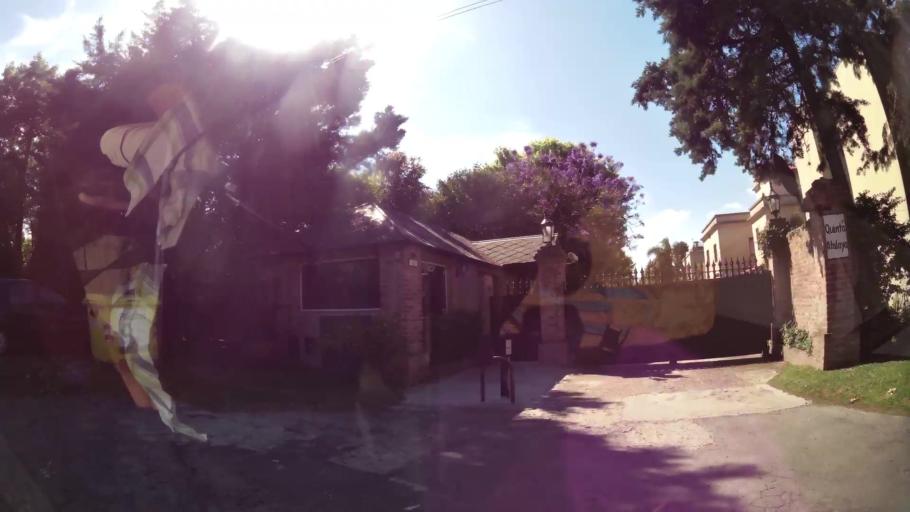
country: AR
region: Buenos Aires
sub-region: Partido de Tigre
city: Tigre
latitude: -34.4874
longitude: -58.5761
